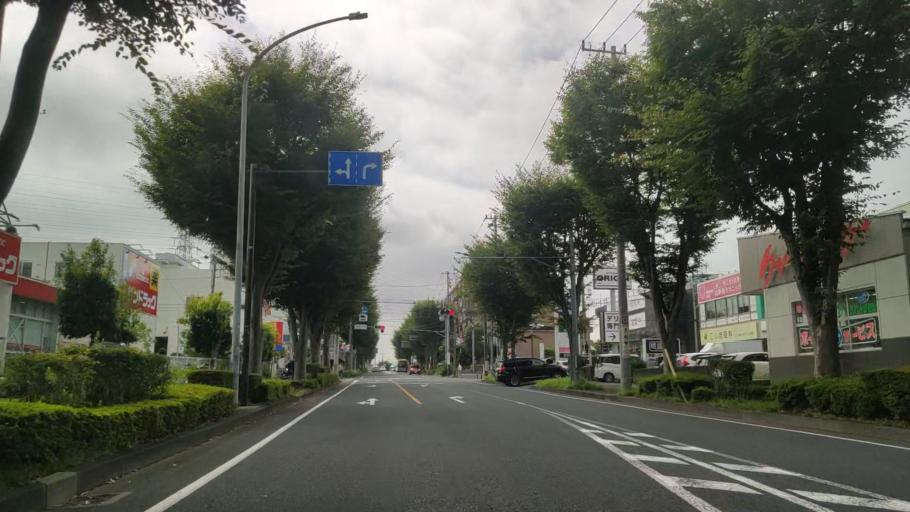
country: JP
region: Kanagawa
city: Fujisawa
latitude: 35.4185
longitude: 139.5232
